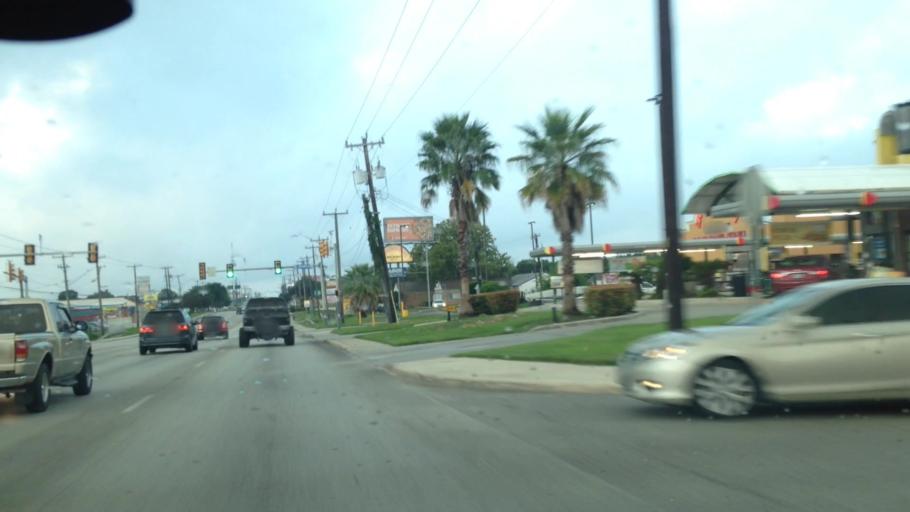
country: US
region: Texas
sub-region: Bexar County
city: Windcrest
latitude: 29.5609
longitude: -98.3942
